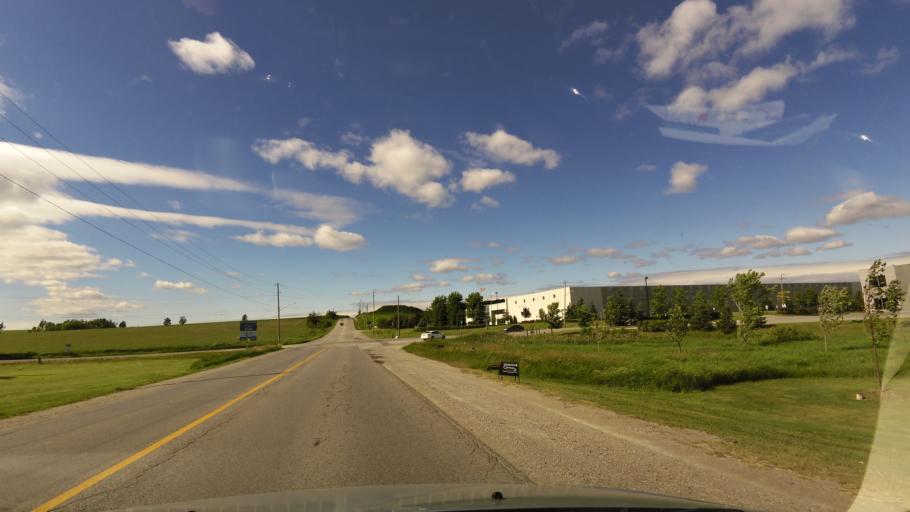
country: CA
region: Ontario
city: Bradford West Gwillimbury
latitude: 44.1174
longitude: -79.6049
